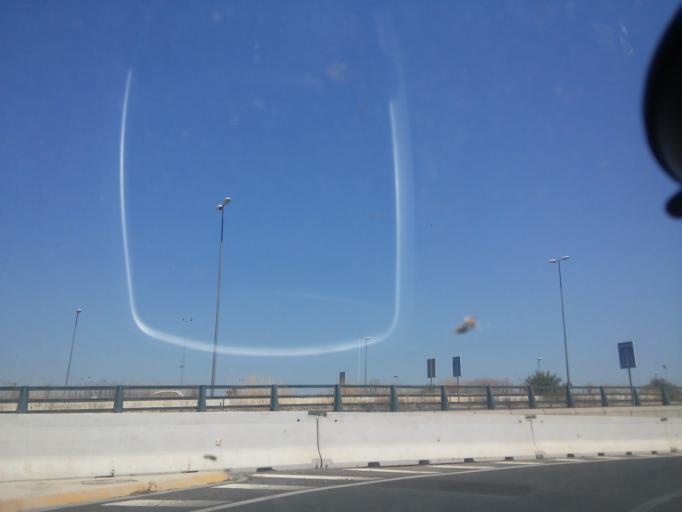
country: ES
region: Andalusia
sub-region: Provincia de Sevilla
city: La Algaba
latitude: 37.4339
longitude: -5.9742
